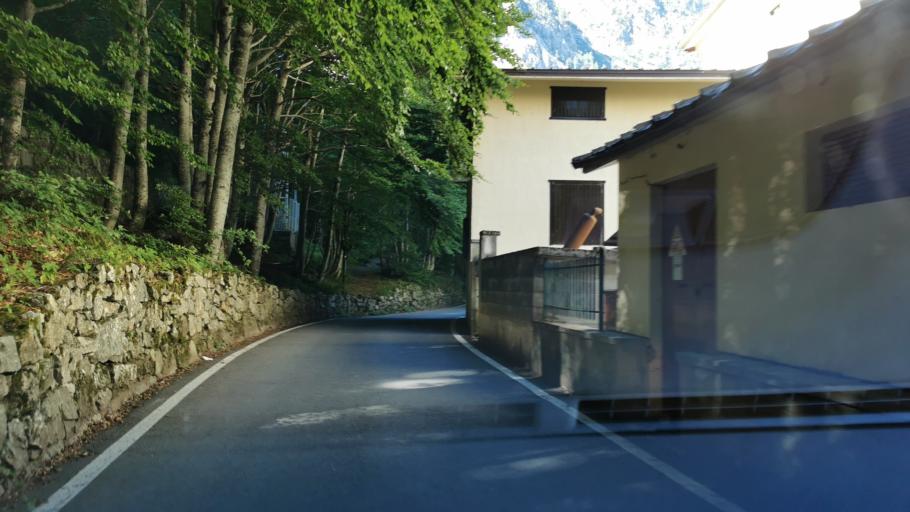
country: IT
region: Piedmont
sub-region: Provincia di Cuneo
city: Demonte
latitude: 44.2072
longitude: 7.2727
